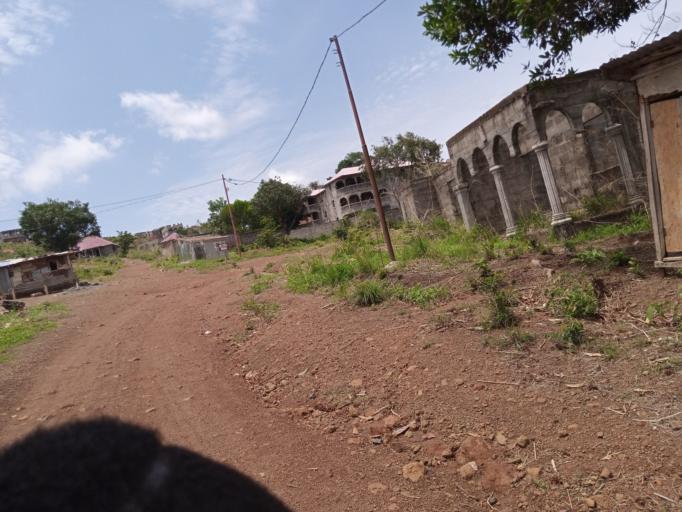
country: SL
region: Western Area
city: Hastings
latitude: 8.3725
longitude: -13.1460
